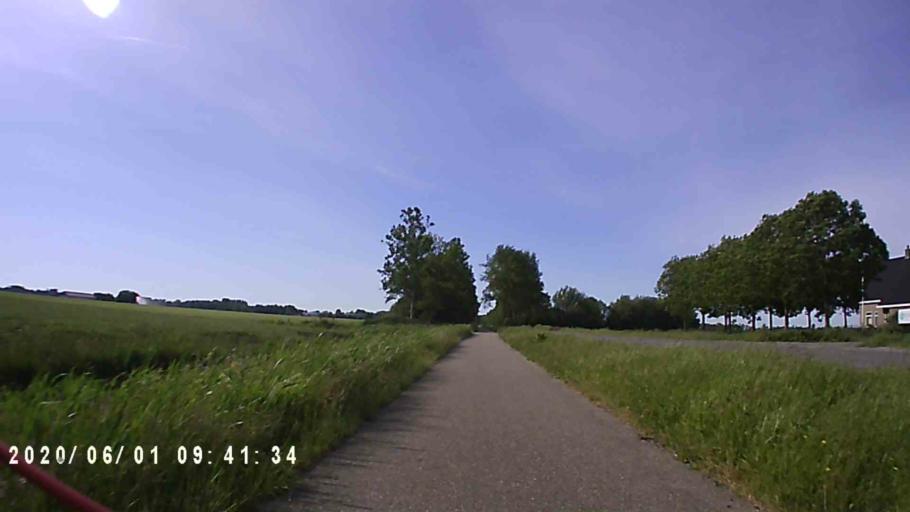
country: NL
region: Friesland
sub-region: Menameradiel
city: Berltsum
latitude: 53.2478
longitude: 5.6822
